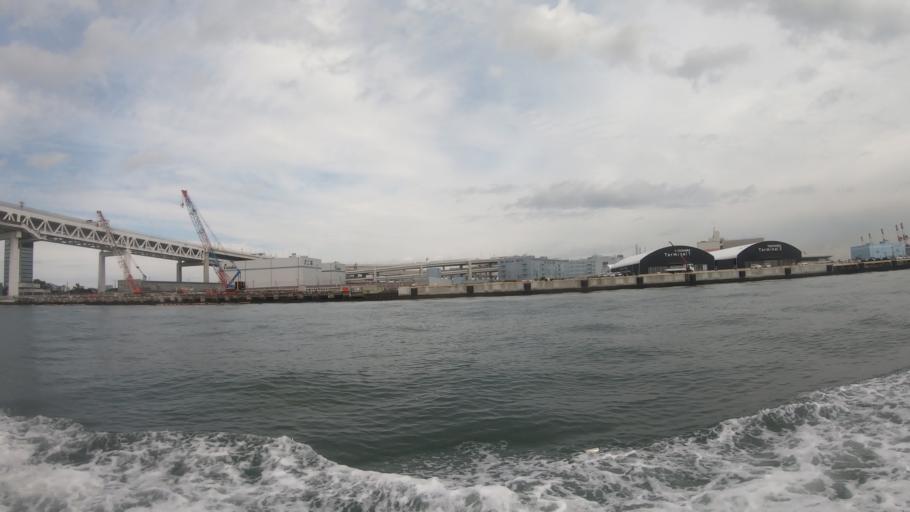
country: JP
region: Kanagawa
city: Yokohama
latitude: 35.4561
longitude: 139.6789
